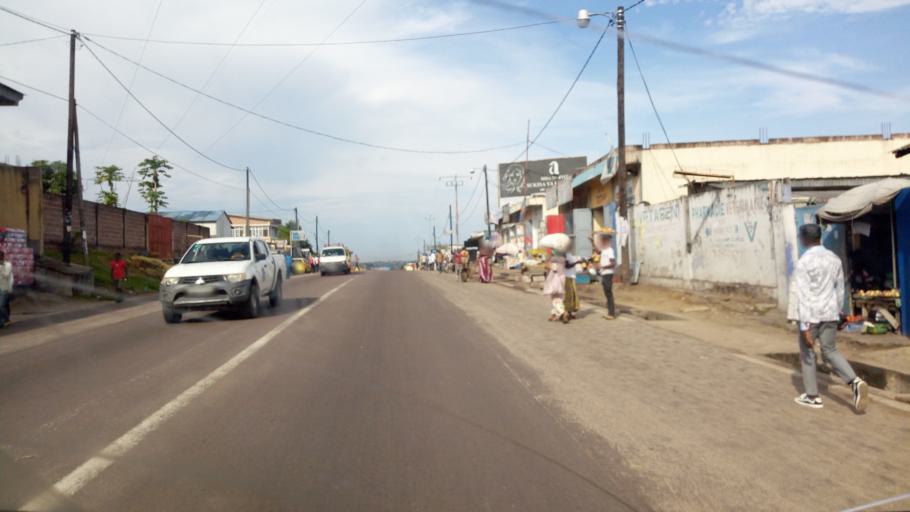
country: CD
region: Kinshasa
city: Kinshasa
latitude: -4.4449
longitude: 15.2523
